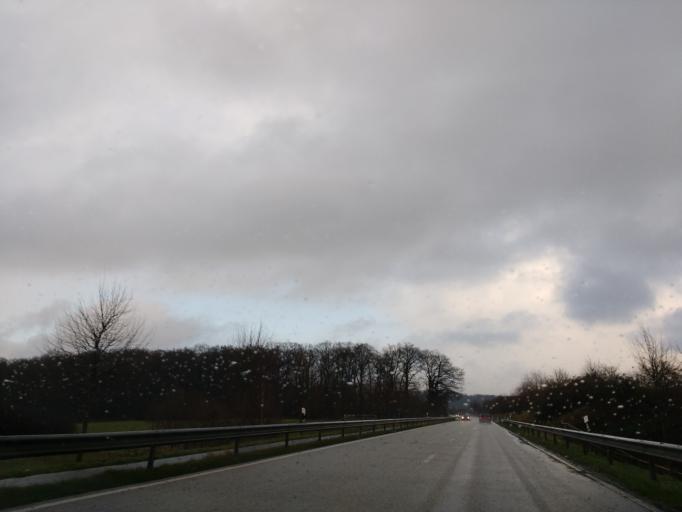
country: DE
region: Schleswig-Holstein
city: Gross Wittensee
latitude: 54.4117
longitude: 9.7852
